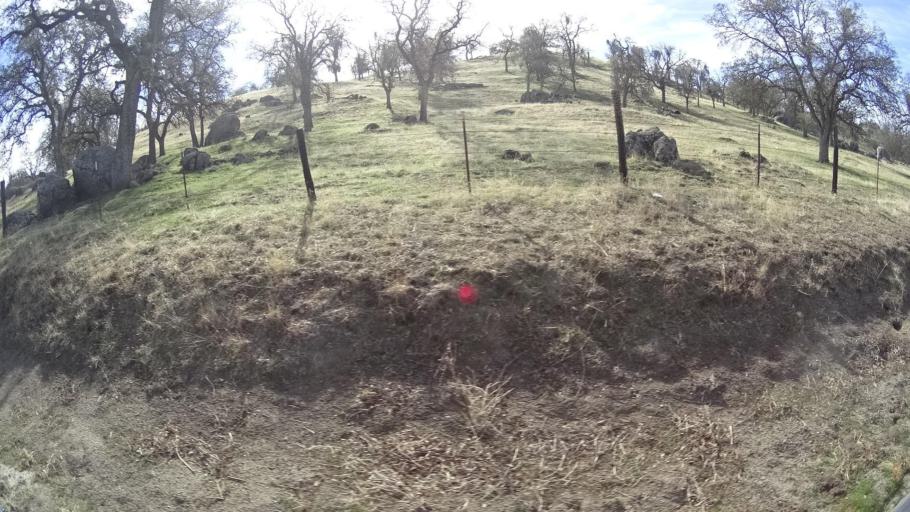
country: US
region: California
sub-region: Kern County
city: Oildale
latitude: 35.6273
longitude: -118.8285
